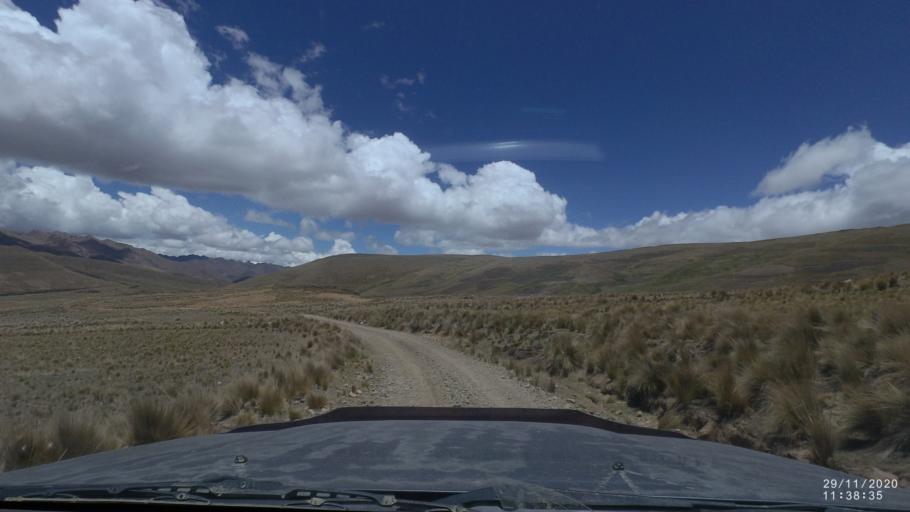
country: BO
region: Cochabamba
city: Cochabamba
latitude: -17.1978
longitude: -66.2355
